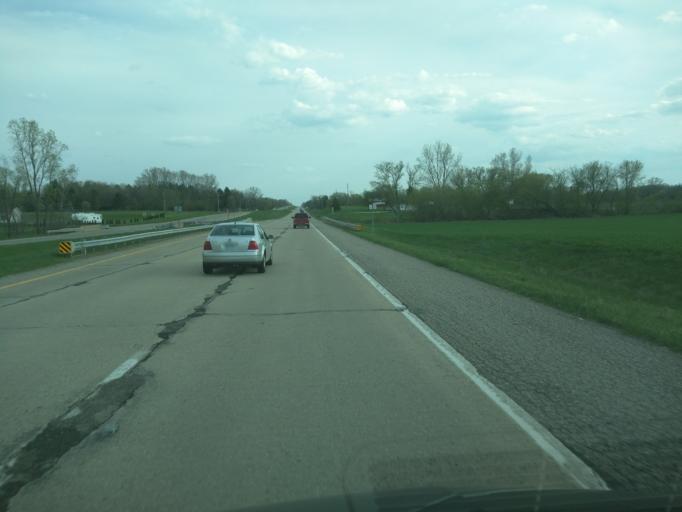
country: US
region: Michigan
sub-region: Eaton County
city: Dimondale
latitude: 42.6198
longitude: -84.6228
